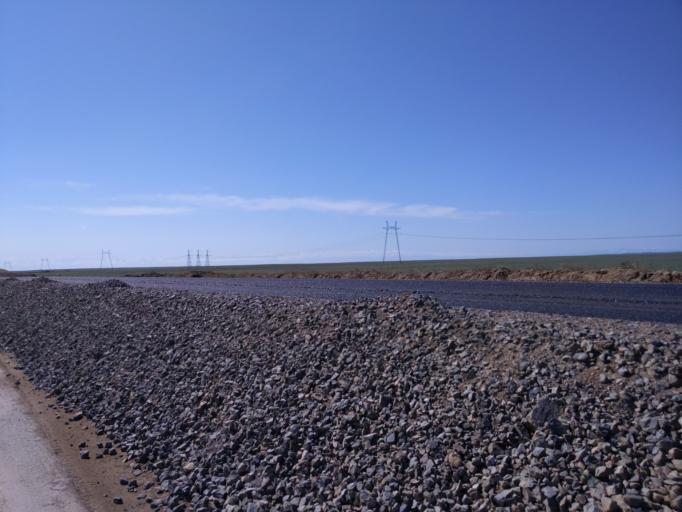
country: KZ
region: Almaty Oblysy
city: Bakanas
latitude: 43.9668
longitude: 76.1995
